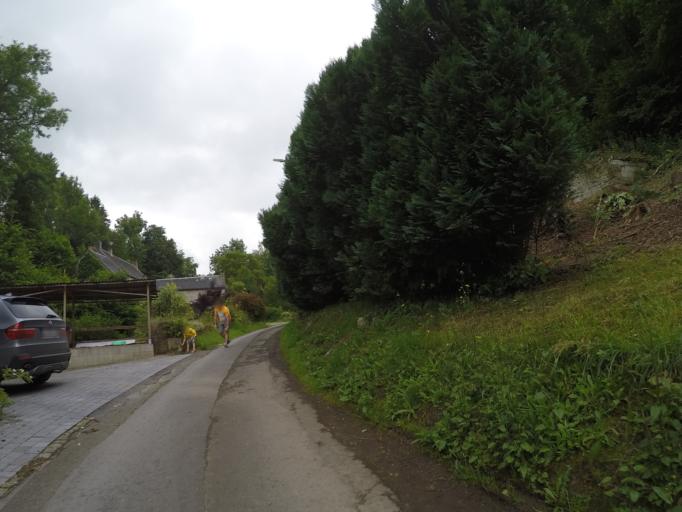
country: BE
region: Wallonia
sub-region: Province de Namur
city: Assesse
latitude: 50.3479
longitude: 4.9558
